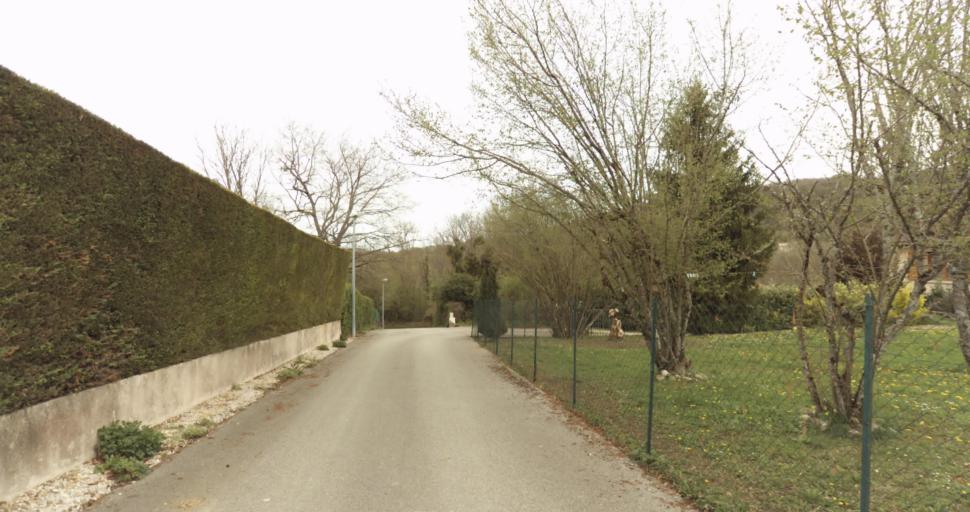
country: FR
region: Rhone-Alpes
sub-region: Departement de l'Ain
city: Amberieu-en-Bugey
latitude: 45.9650
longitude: 5.3707
